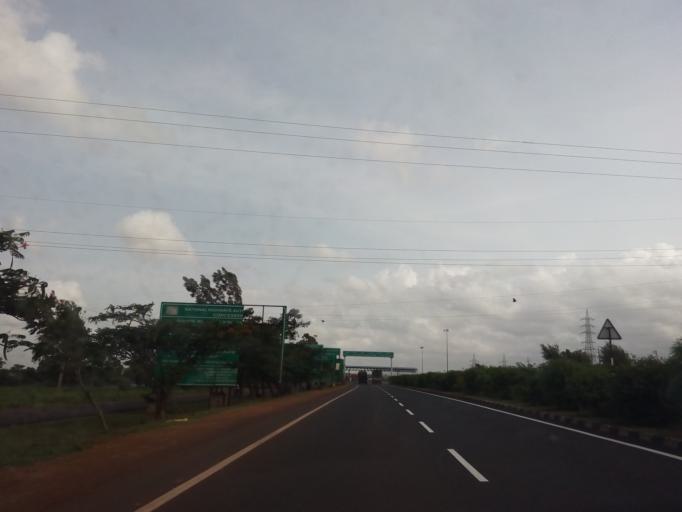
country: IN
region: Karnataka
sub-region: Belgaum
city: Sankeshwar
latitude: 16.1468
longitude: 74.5172
